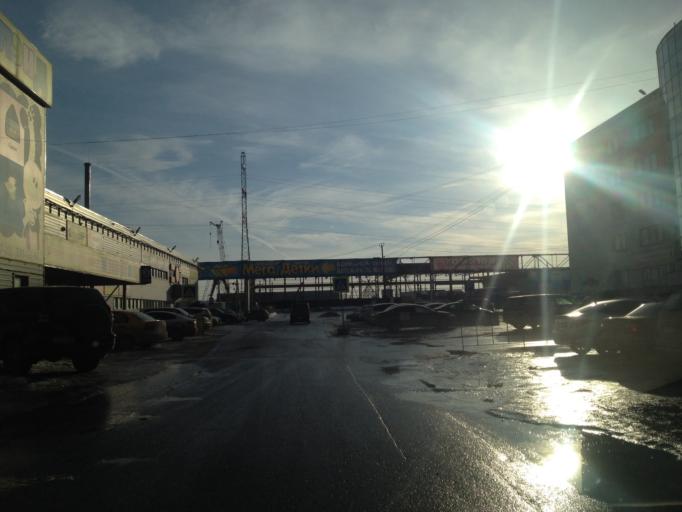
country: RU
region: Sverdlovsk
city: Istok
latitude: 56.7568
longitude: 60.7564
